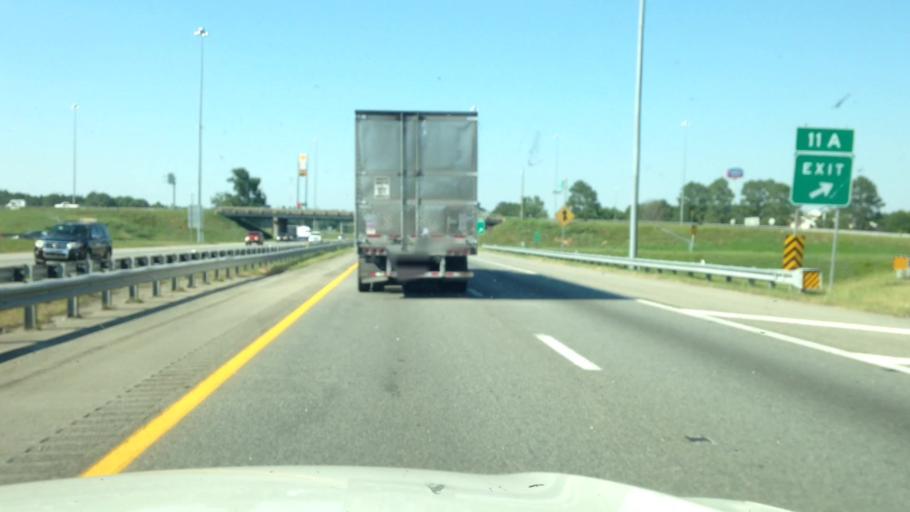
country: US
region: Virginia
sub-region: City of Emporia
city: Emporia
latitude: 36.7010
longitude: -77.5503
